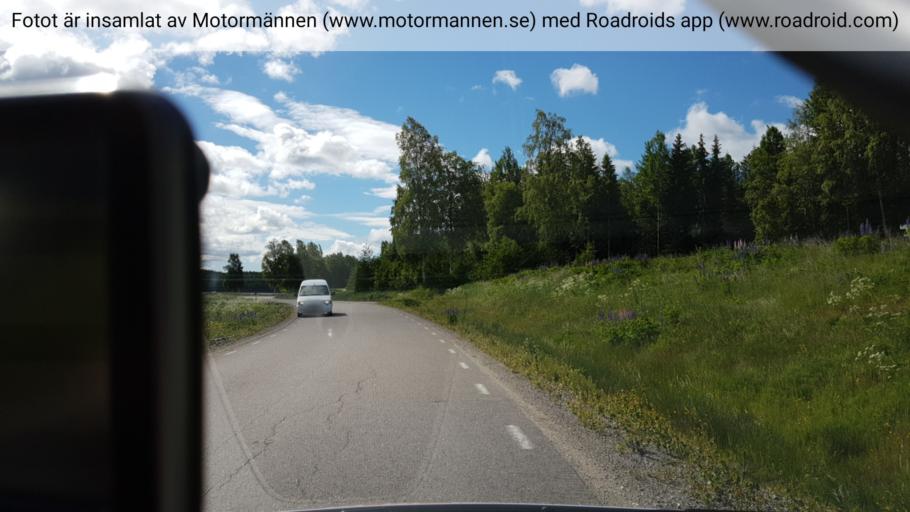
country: SE
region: Gaevleborg
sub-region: Hudiksvalls Kommun
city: Sorforsa
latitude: 61.6676
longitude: 16.9248
